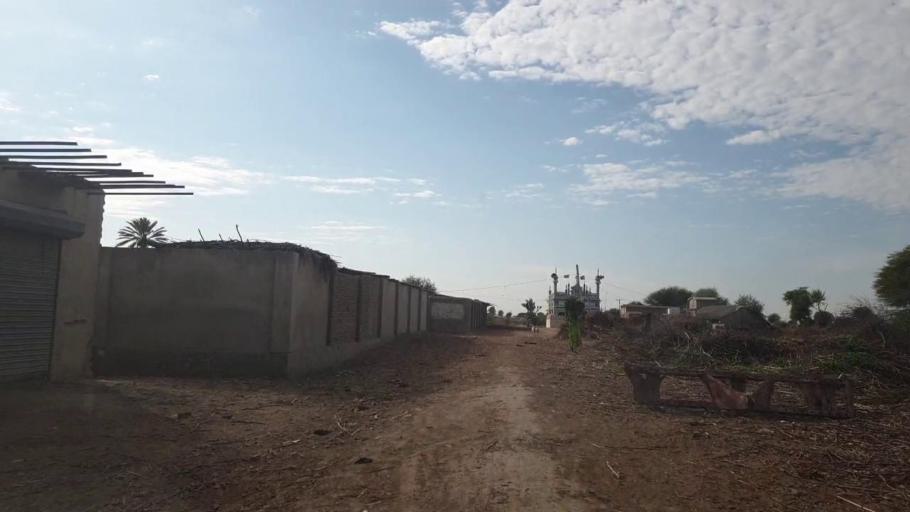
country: PK
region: Sindh
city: Sinjhoro
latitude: 26.0648
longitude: 68.8716
